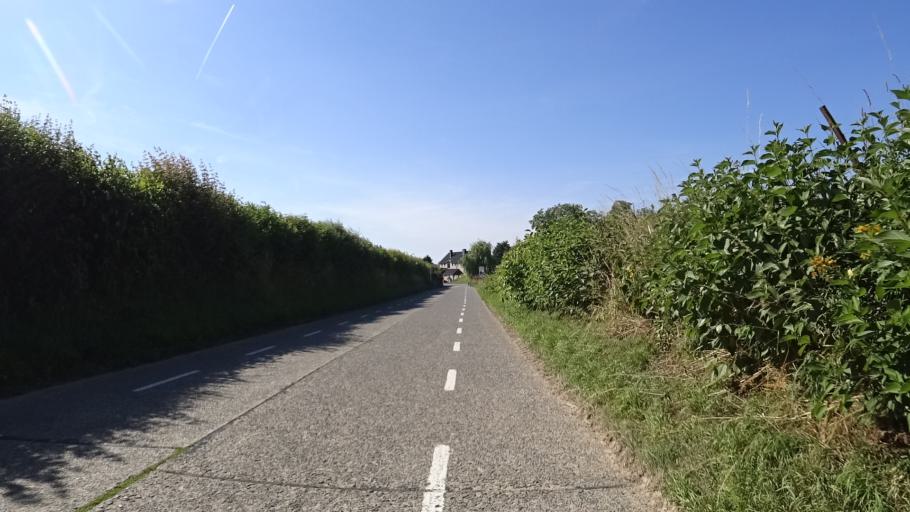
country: BE
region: Wallonia
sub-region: Province du Brabant Wallon
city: Incourt
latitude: 50.6679
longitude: 4.8074
